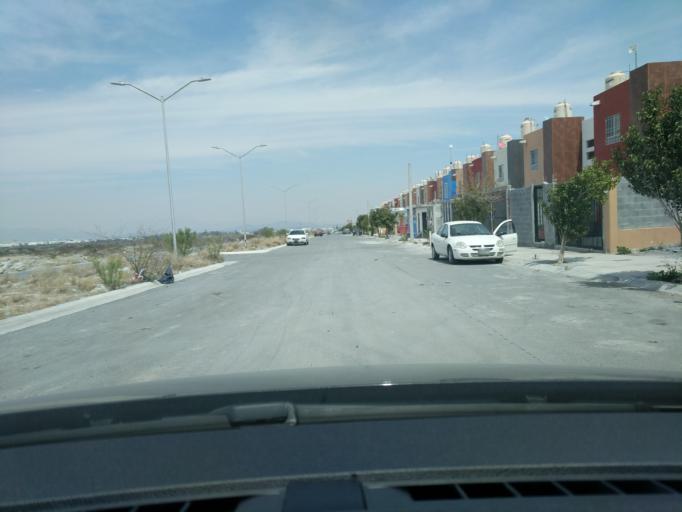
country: MX
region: Coahuila
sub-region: Arteaga
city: Arteaga
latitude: 25.4216
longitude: -100.9113
